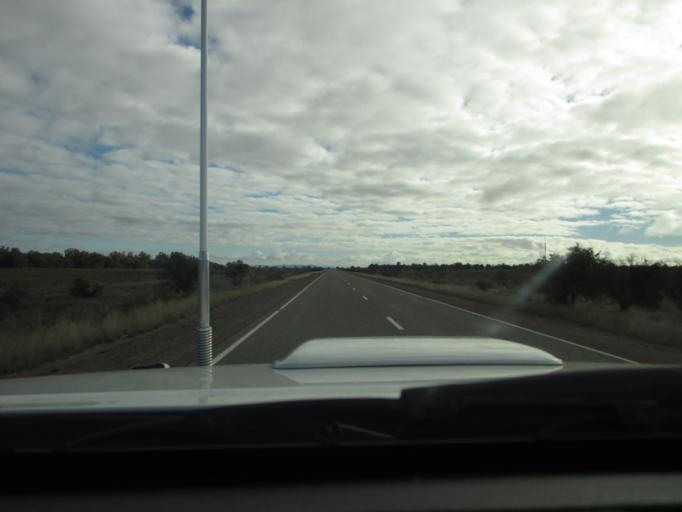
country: AU
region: South Australia
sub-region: Flinders Ranges
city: Quorn
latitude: -32.4710
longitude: 138.5399
